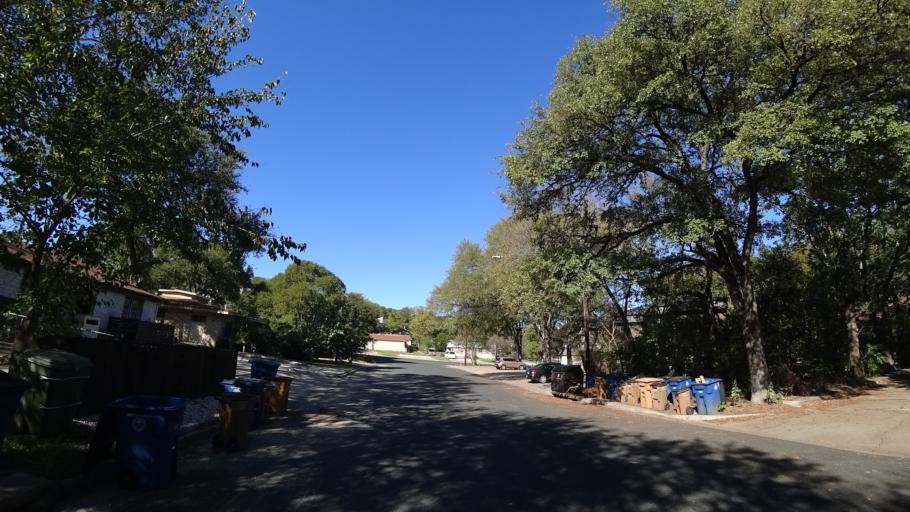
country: US
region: Texas
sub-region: Travis County
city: Rollingwood
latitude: 30.2403
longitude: -97.7809
